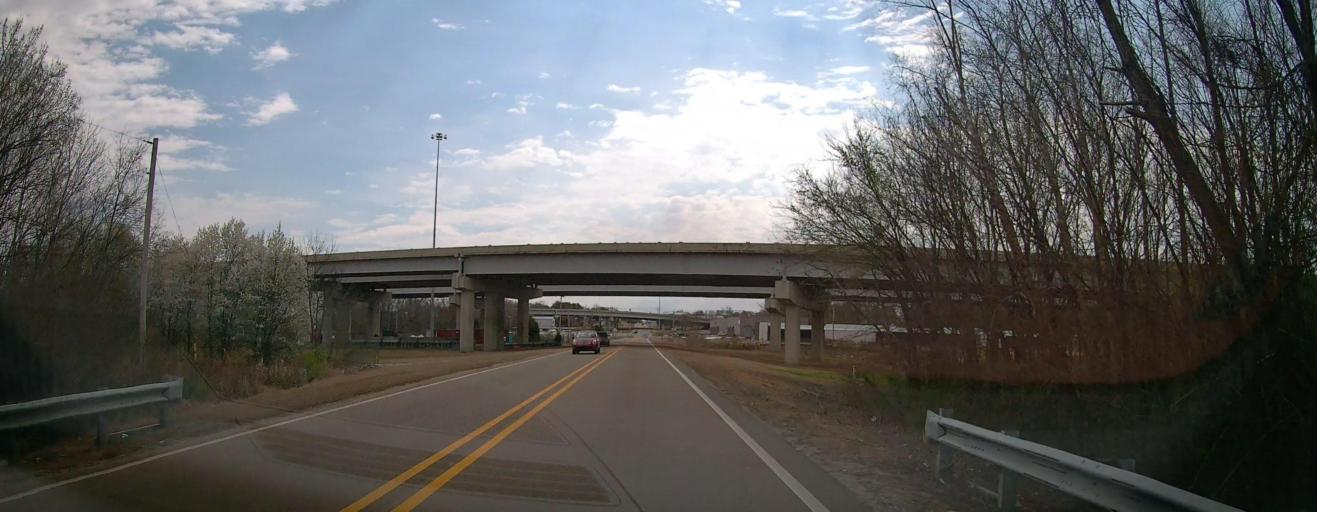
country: US
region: Mississippi
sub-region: De Soto County
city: Olive Branch
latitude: 34.9685
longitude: -89.8347
